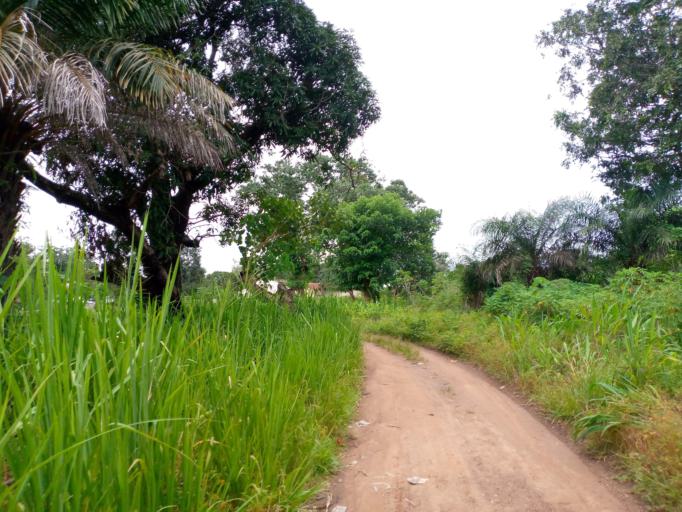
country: SL
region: Northern Province
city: Magburaka
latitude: 8.7242
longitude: -11.9323
